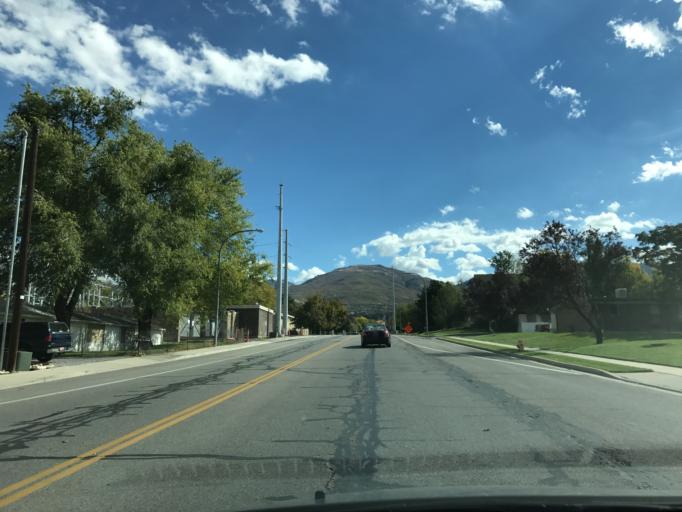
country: US
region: Utah
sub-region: Davis County
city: Woods Cross
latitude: 40.8711
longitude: -111.8879
